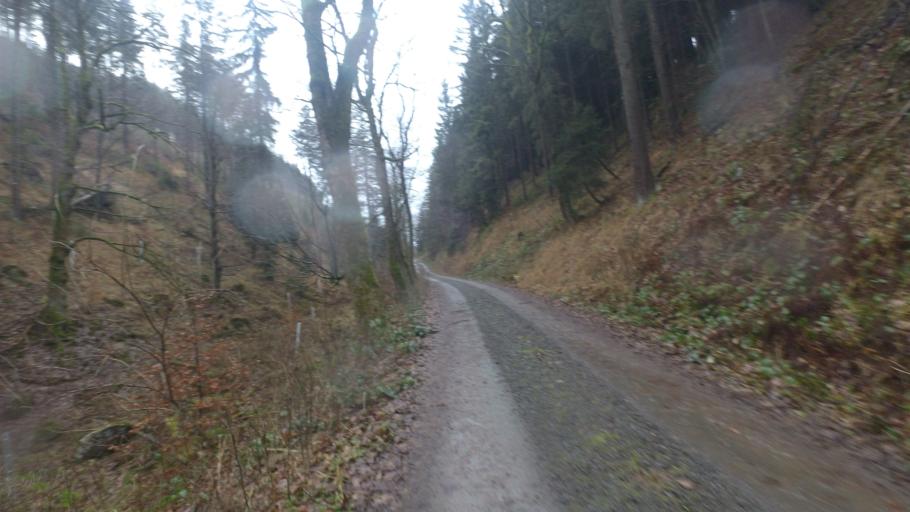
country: DE
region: Thuringia
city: Frankenhain
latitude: 50.7180
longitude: 10.7715
